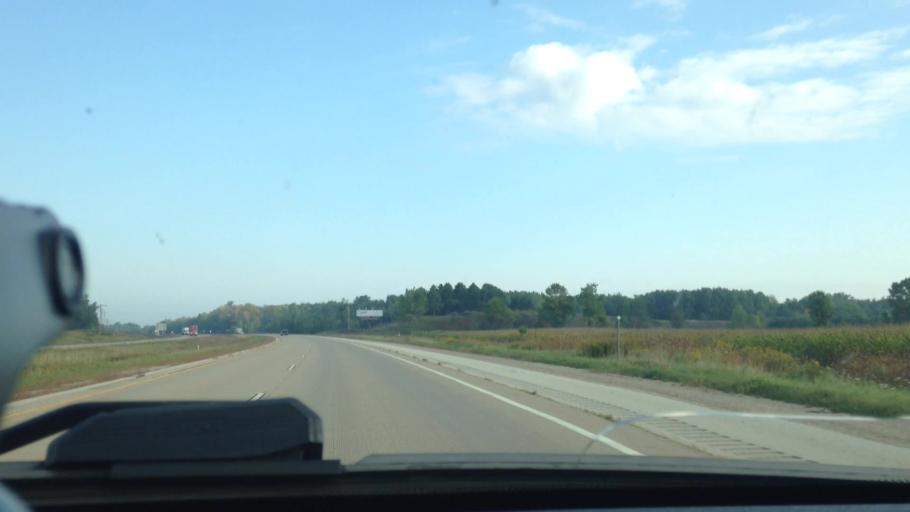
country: US
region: Wisconsin
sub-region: Oconto County
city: Oconto Falls
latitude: 44.9660
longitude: -88.0355
